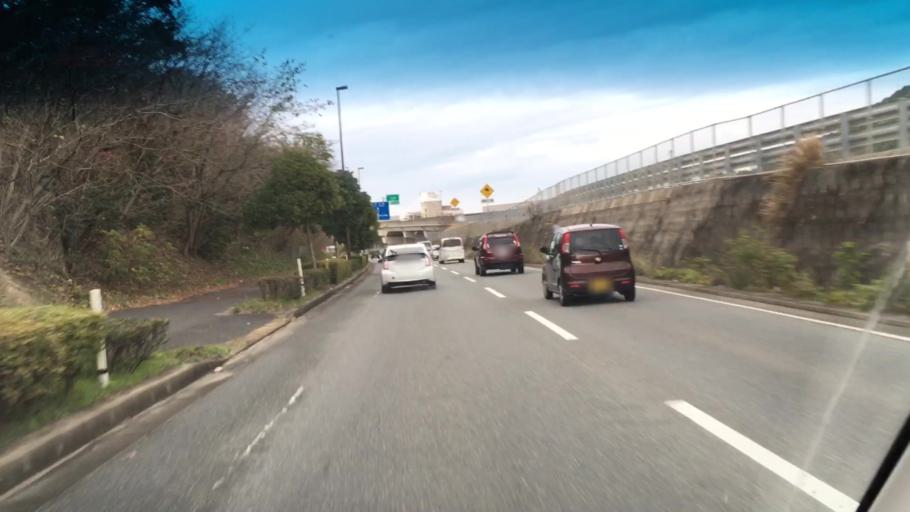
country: JP
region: Fukuoka
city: Maebaru-chuo
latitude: 33.5711
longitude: 130.2885
